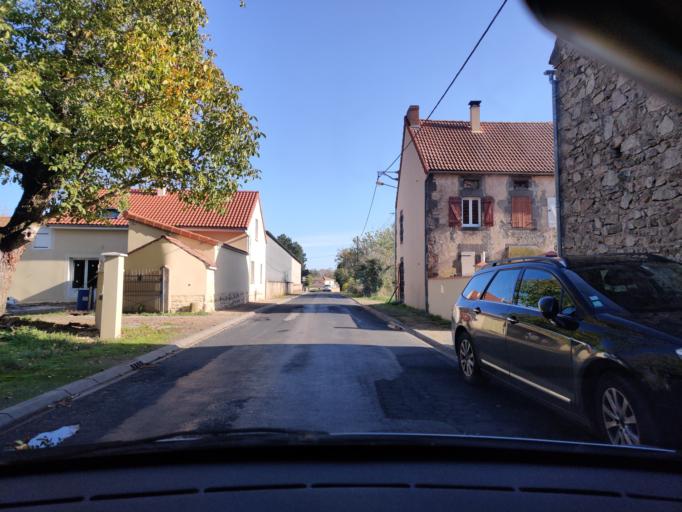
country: FR
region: Auvergne
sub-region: Departement du Puy-de-Dome
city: Combronde
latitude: 46.0398
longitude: 3.1281
